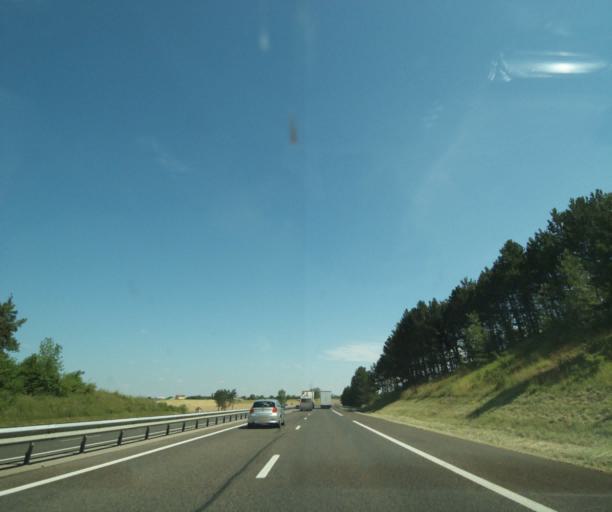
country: FR
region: Lorraine
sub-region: Departement de Meurthe-et-Moselle
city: Colombey-les-Belles
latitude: 48.5739
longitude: 5.8864
